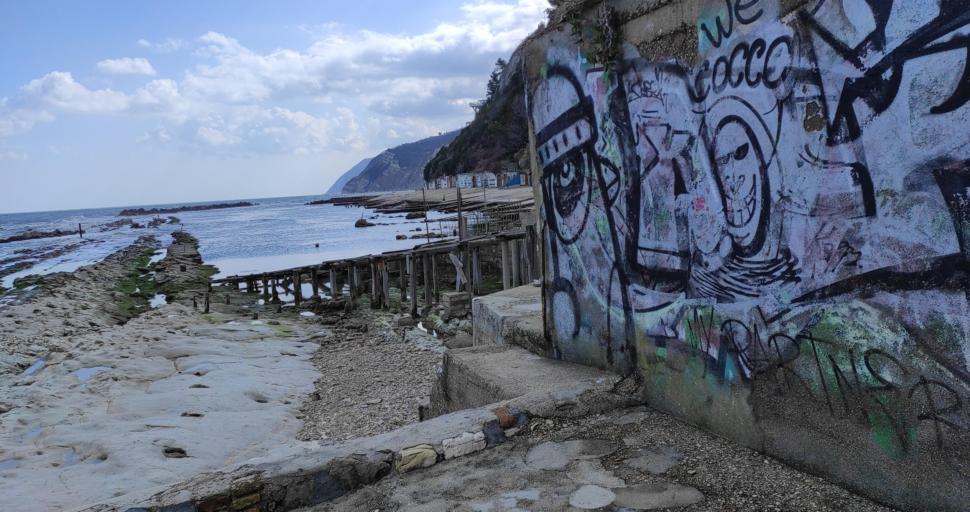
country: IT
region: The Marches
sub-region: Provincia di Ancona
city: Pietra la Croce
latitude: 43.6191
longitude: 13.5315
